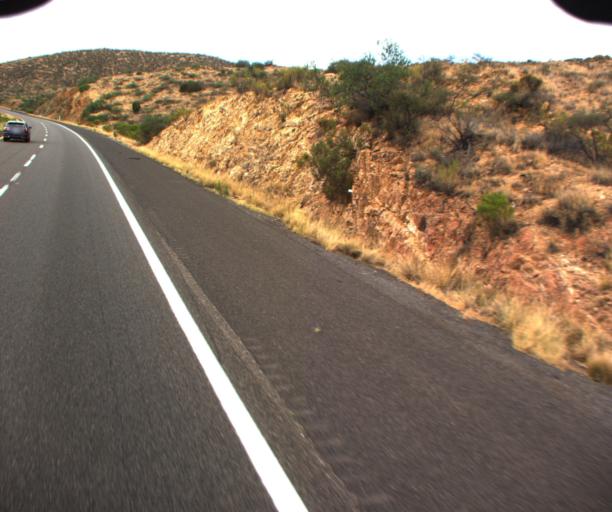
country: US
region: Arizona
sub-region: Yavapai County
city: Cordes Lakes
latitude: 34.3076
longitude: -112.1271
